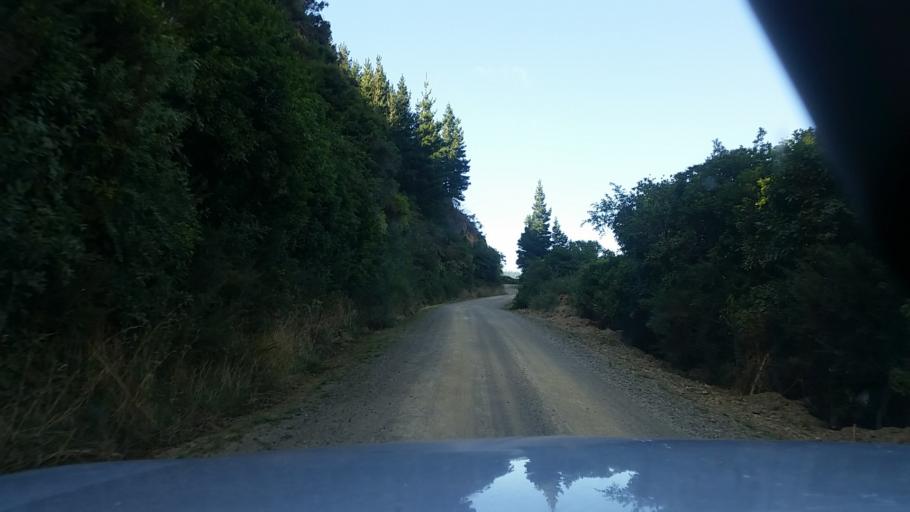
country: NZ
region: Marlborough
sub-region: Marlborough District
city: Picton
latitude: -41.2892
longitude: 174.1669
